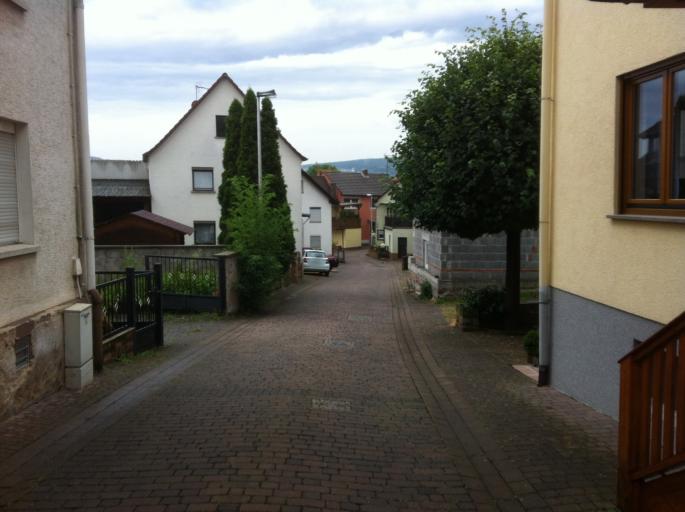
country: DE
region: Bavaria
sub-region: Regierungsbezirk Unterfranken
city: Eschau
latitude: 49.8187
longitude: 9.2563
